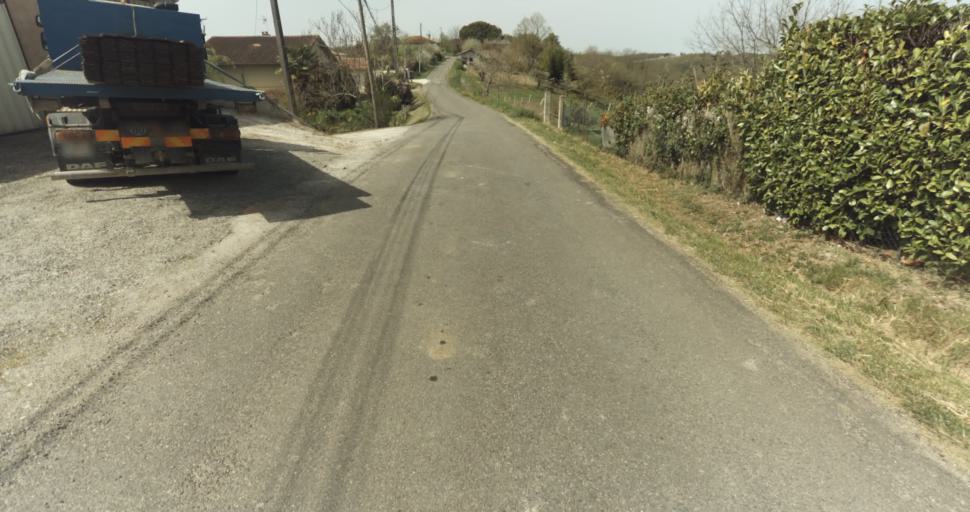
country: FR
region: Midi-Pyrenees
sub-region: Departement du Tarn-et-Garonne
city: Moissac
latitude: 44.1302
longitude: 1.0805
